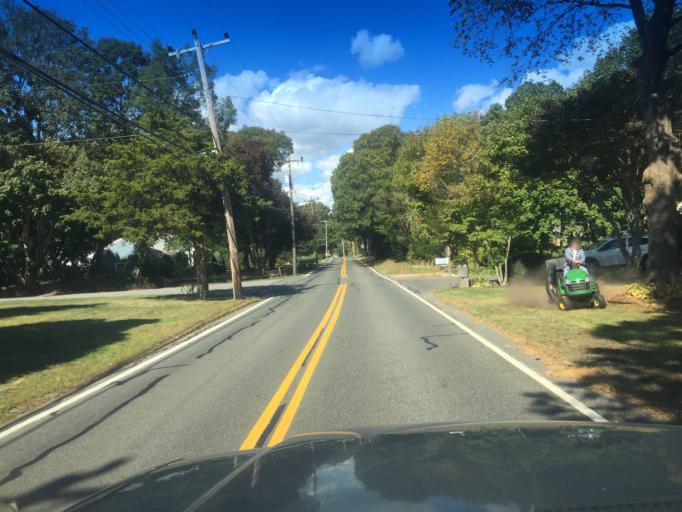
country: US
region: Massachusetts
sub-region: Barnstable County
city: Pocasset
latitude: 41.6822
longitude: -70.6142
